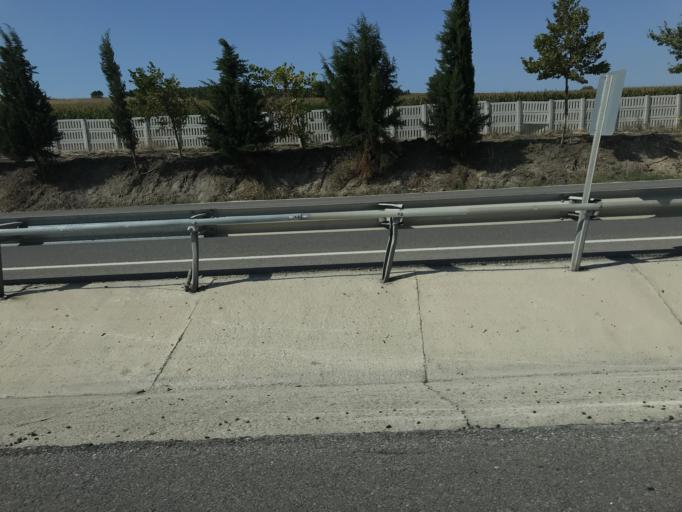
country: TR
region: Bursa
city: Mahmudiye
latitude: 40.2084
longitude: 28.5996
